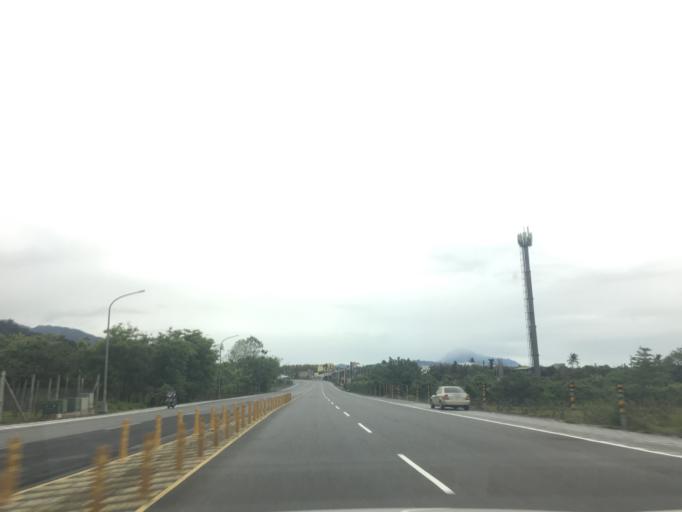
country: TW
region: Taiwan
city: Taitung City
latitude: 22.7236
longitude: 121.0550
